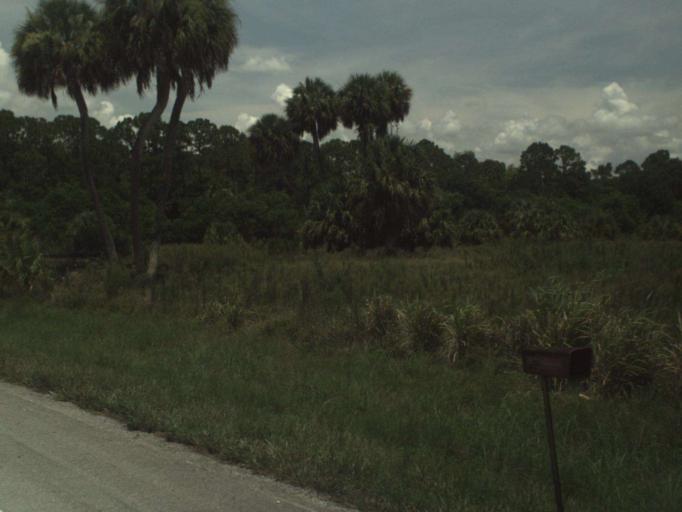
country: US
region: Florida
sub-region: Saint Lucie County
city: Lakewood Park
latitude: 27.5211
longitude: -80.4097
